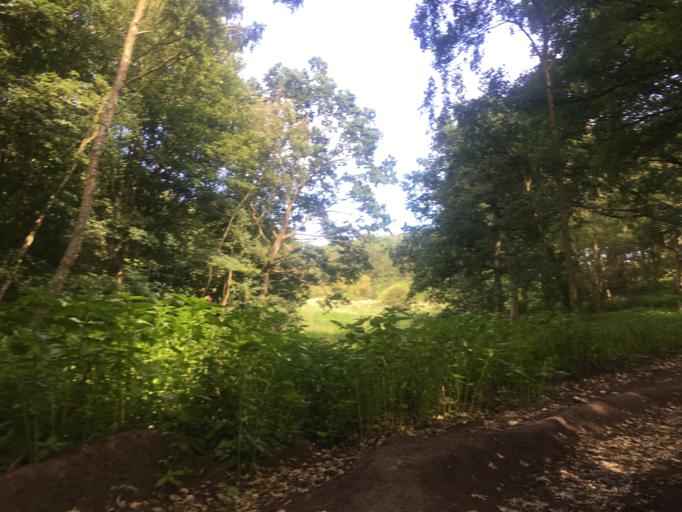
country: GB
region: England
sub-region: Sunderland
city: Washington
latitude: 54.8768
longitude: -1.5297
